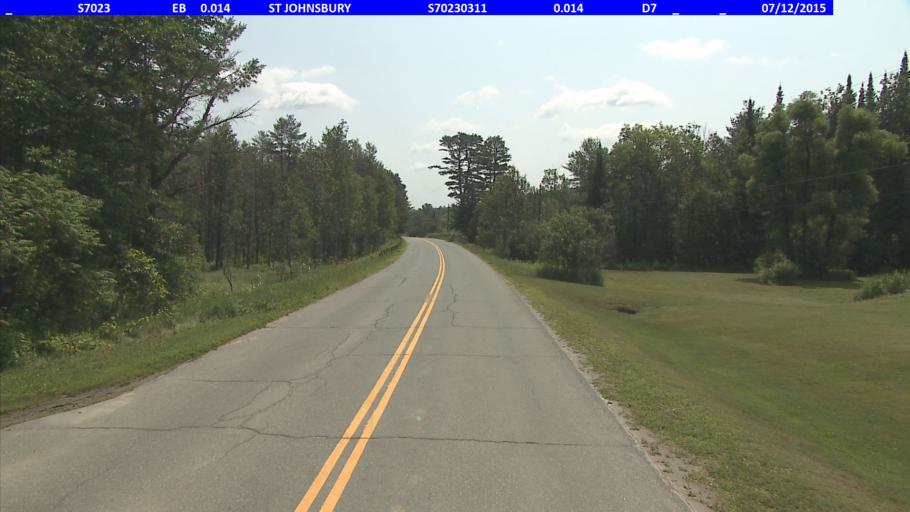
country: US
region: Vermont
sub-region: Caledonia County
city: St Johnsbury
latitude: 44.4482
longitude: -72.0620
